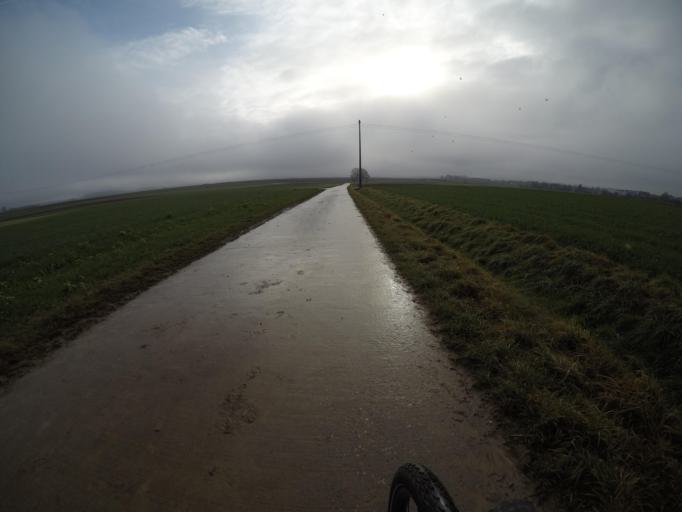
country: DE
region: Baden-Wuerttemberg
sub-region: Regierungsbezirk Stuttgart
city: Wolfschlugen
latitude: 48.6519
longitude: 9.2588
